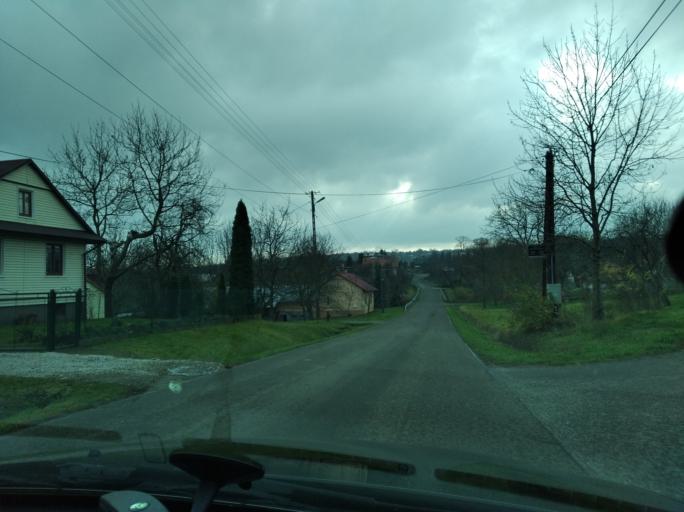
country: PL
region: Subcarpathian Voivodeship
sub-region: Powiat przeworski
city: Sietesz
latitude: 49.9859
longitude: 22.3468
